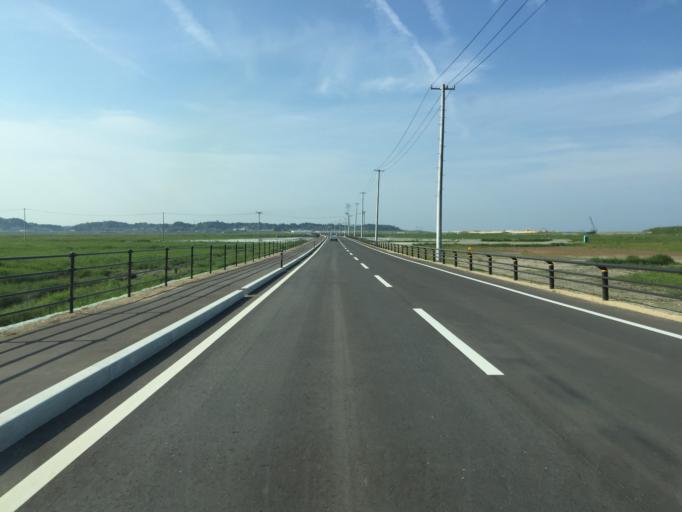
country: JP
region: Fukushima
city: Namie
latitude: 37.6892
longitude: 141.0054
